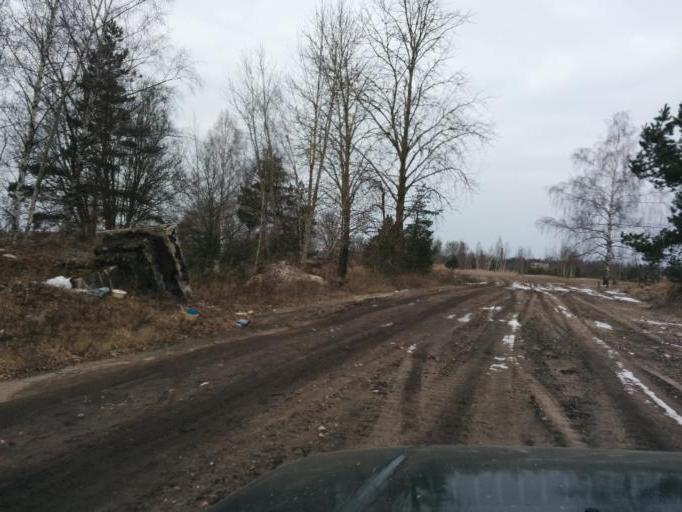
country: LV
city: Tireli
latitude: 56.9382
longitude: 23.6457
